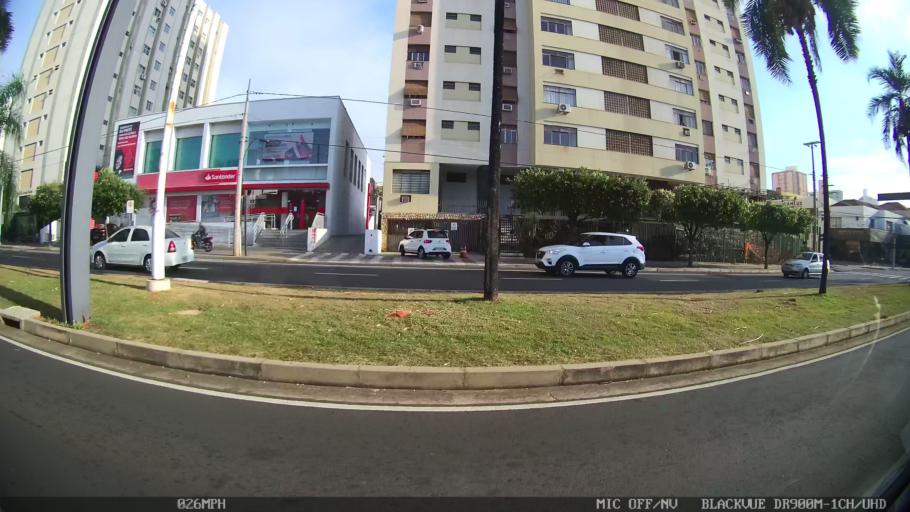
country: BR
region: Sao Paulo
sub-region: Sao Jose Do Rio Preto
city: Sao Jose do Rio Preto
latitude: -20.8153
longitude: -49.3797
